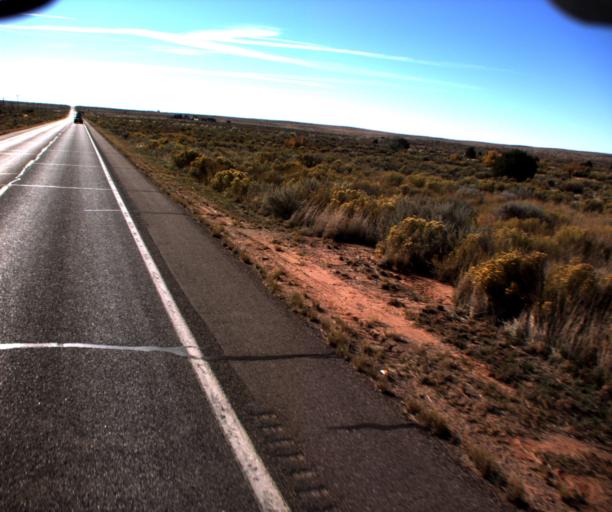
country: US
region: Arizona
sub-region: Mohave County
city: Colorado City
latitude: 36.9301
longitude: -112.9430
